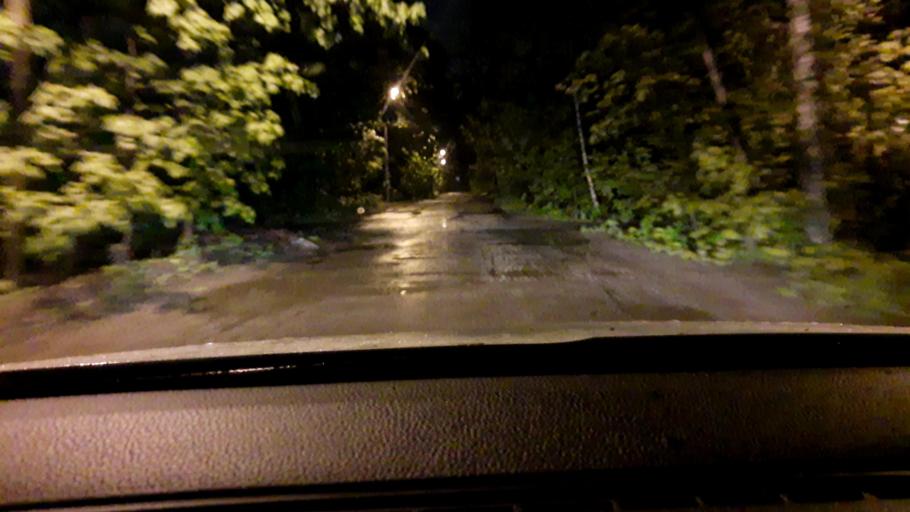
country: RU
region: Moskovskaya
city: Ivanteyevka
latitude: 55.9543
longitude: 37.9314
